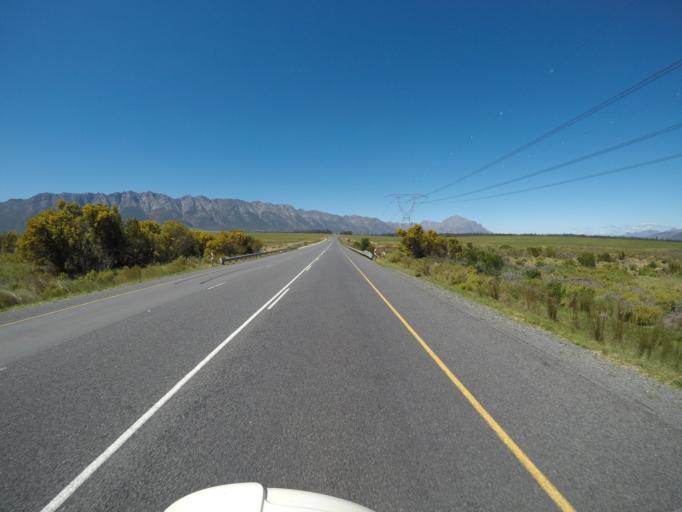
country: ZA
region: Western Cape
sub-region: Cape Winelands District Municipality
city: Ceres
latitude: -33.3239
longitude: 19.1469
